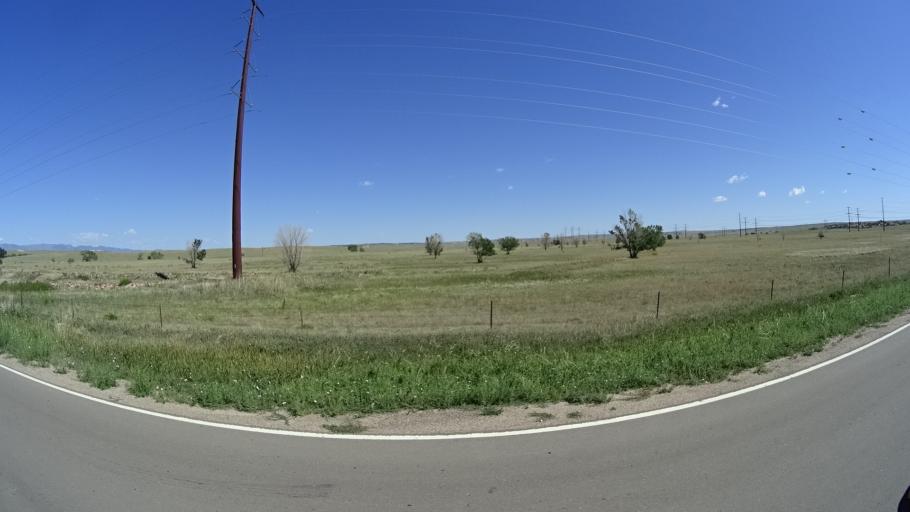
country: US
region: Colorado
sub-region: El Paso County
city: Security-Widefield
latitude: 38.7810
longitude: -104.6337
